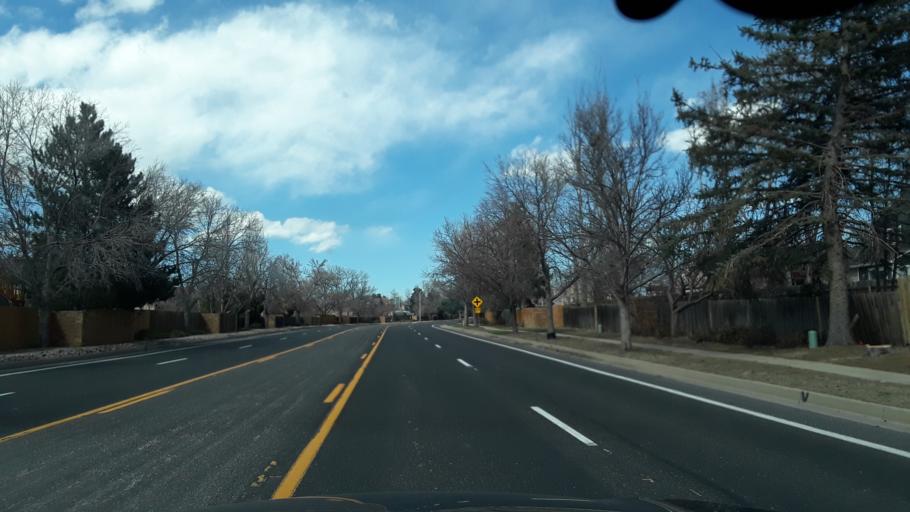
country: US
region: Colorado
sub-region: El Paso County
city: Black Forest
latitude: 38.9529
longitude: -104.7512
